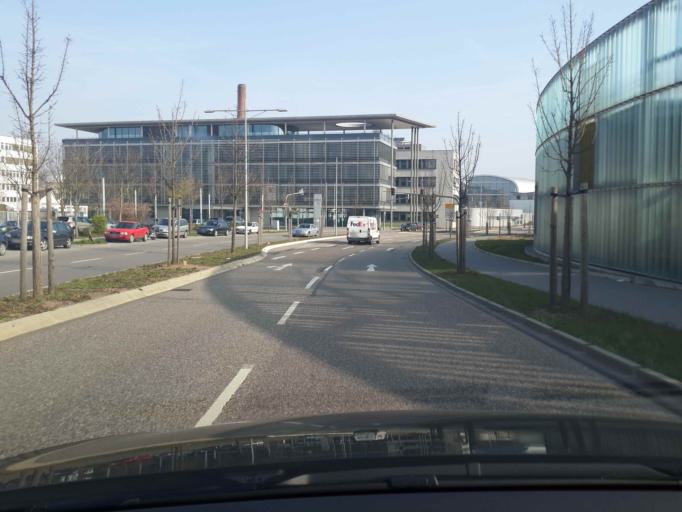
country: DE
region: Baden-Wuerttemberg
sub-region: Regierungsbezirk Stuttgart
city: Neckarsulm
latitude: 49.1913
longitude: 9.2207
